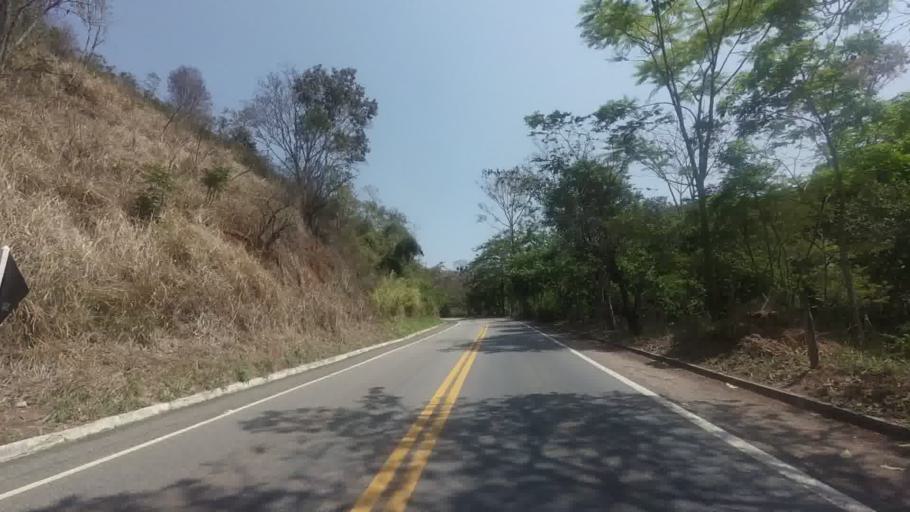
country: BR
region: Espirito Santo
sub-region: Cachoeiro De Itapemirim
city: Cachoeiro de Itapemirim
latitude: -20.8398
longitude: -41.2327
